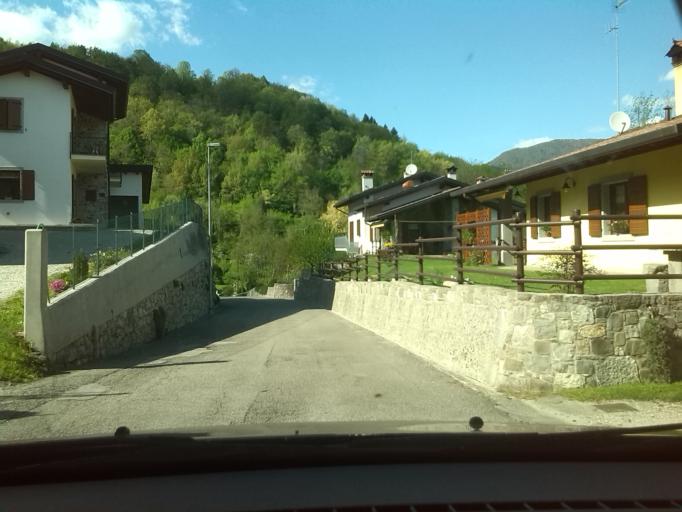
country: IT
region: Friuli Venezia Giulia
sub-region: Provincia di Udine
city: Pulfero
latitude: 46.1487
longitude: 13.4821
